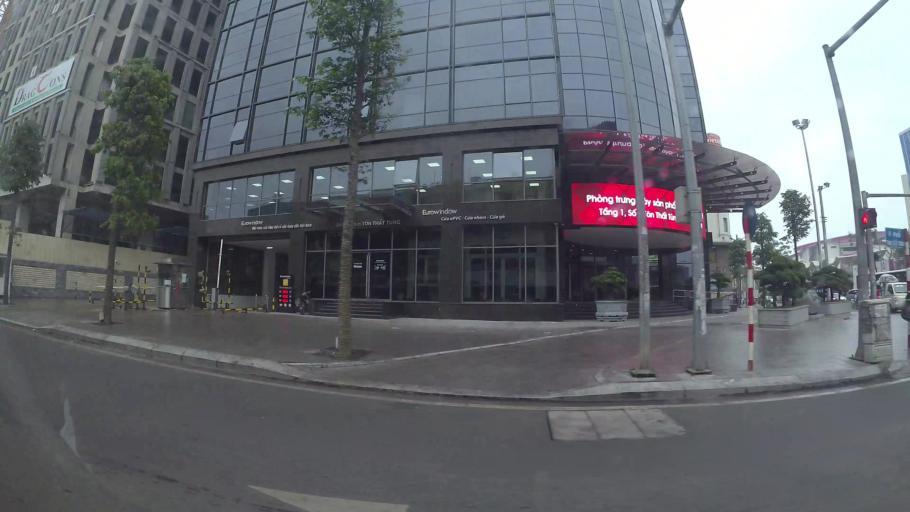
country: VN
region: Ha Noi
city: Dong Da
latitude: 21.0059
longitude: 105.8310
